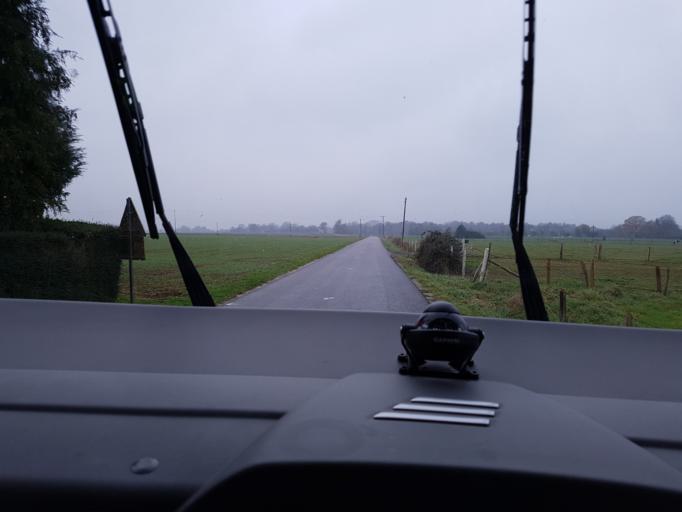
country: FR
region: Haute-Normandie
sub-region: Departement de l'Eure
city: Pont-Audemer
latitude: 49.3985
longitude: 0.5277
